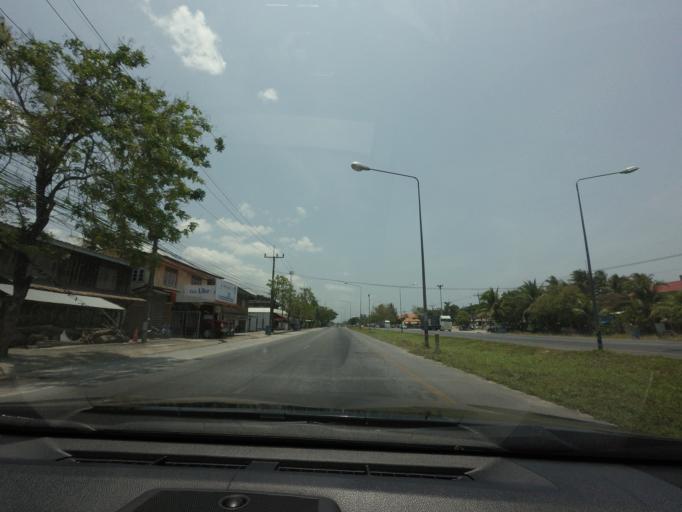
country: TH
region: Pattani
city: Pattani
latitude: 6.8724
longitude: 101.2944
